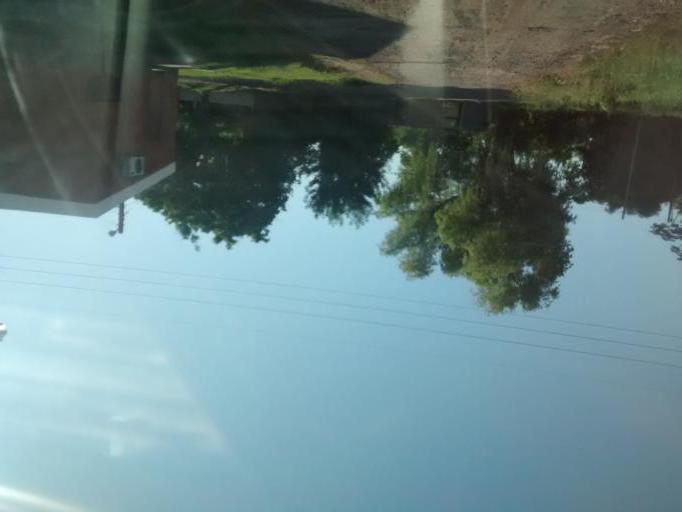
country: AR
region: Chaco
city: Resistencia
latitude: -27.4608
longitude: -58.9709
